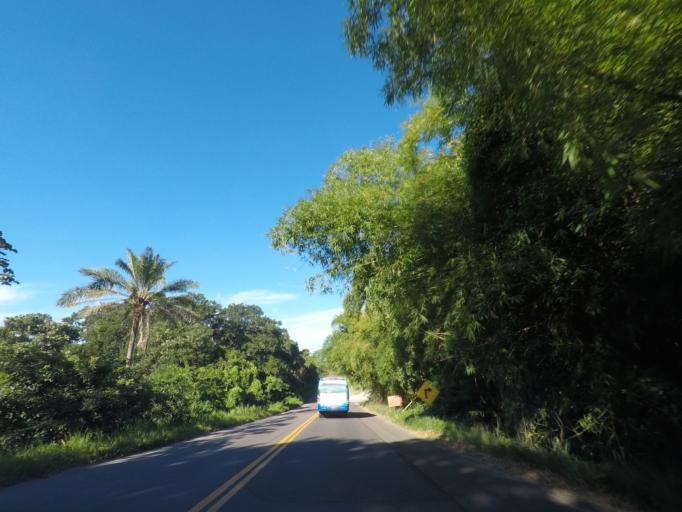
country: BR
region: Bahia
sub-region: Nazare
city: Nazare
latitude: -13.0269
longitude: -39.0012
